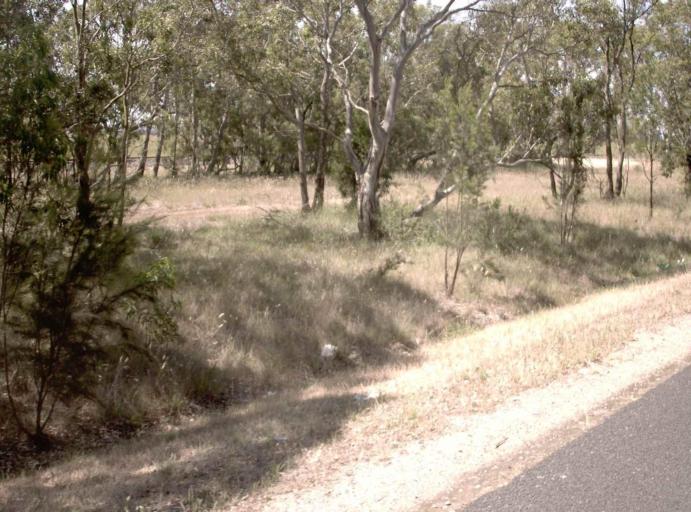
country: AU
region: Victoria
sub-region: Wellington
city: Sale
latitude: -37.9545
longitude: 147.1031
